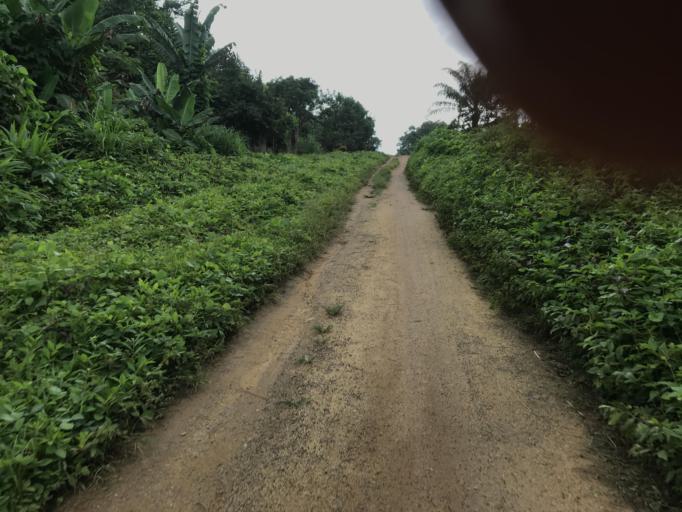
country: GN
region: Nzerekore
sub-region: Prefecture de Guekedou
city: Gueckedou
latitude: 8.4726
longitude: -10.2837
